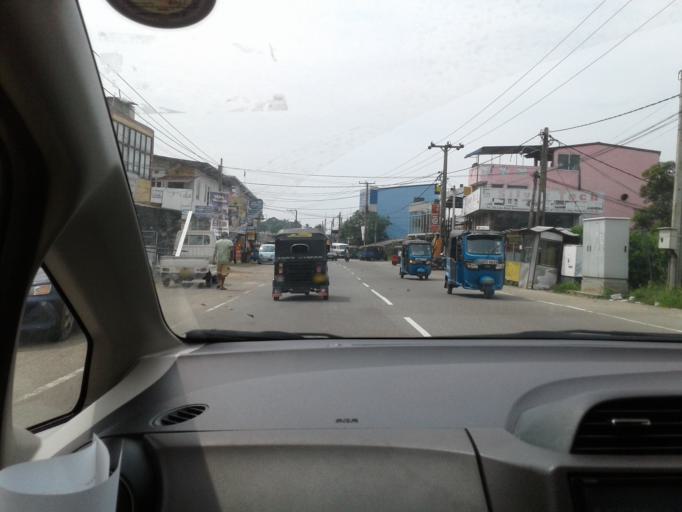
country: LK
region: Western
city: Maharagama
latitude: 6.8434
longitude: 79.9139
